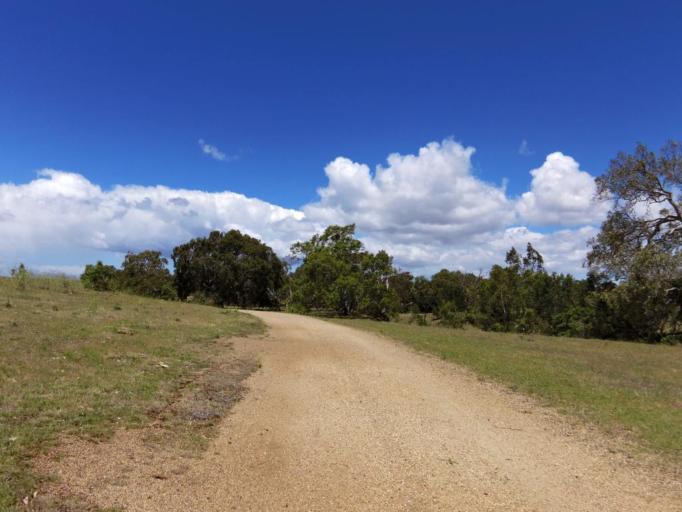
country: AU
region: Victoria
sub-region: Hume
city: Greenvale
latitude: -37.6503
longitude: 144.8464
